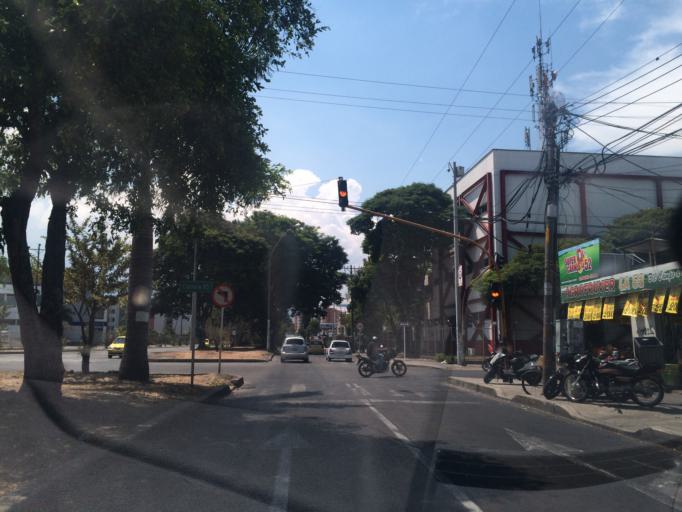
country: CO
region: Valle del Cauca
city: Cali
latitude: 3.4714
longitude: -76.5027
